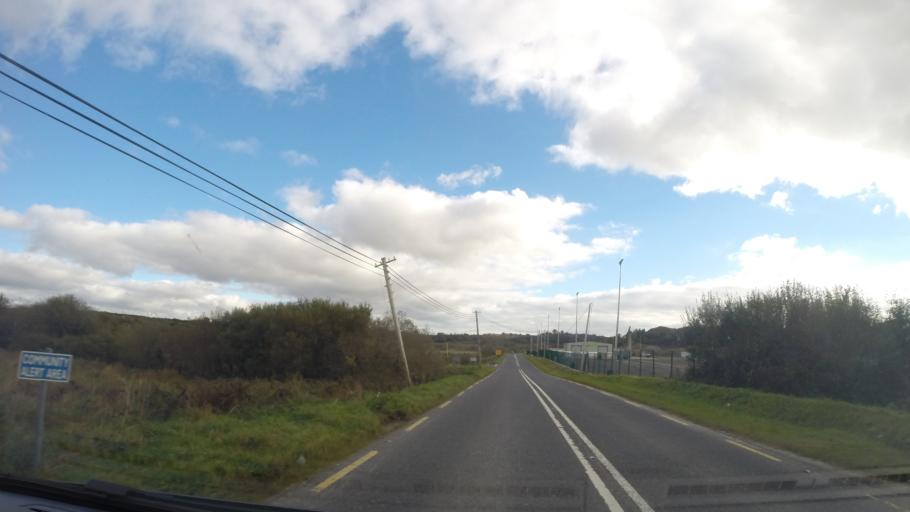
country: IE
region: Ulster
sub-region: County Donegal
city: Killybegs
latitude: 54.6607
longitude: -8.4016
